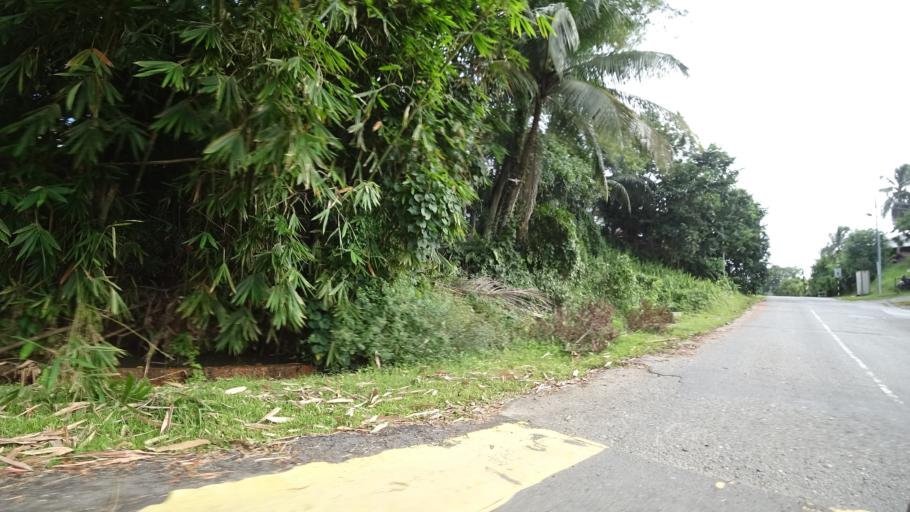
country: BN
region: Brunei and Muara
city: Bandar Seri Begawan
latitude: 4.8925
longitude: 114.9274
